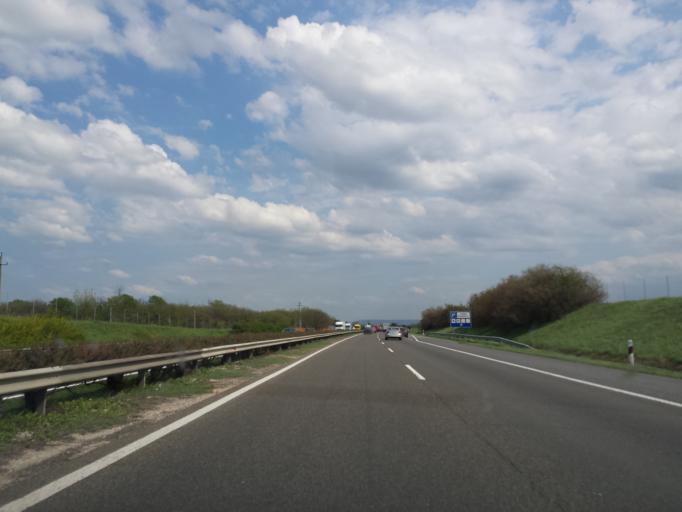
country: HU
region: Komarom-Esztergom
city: Nagyigmand
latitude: 47.6742
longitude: 18.1065
